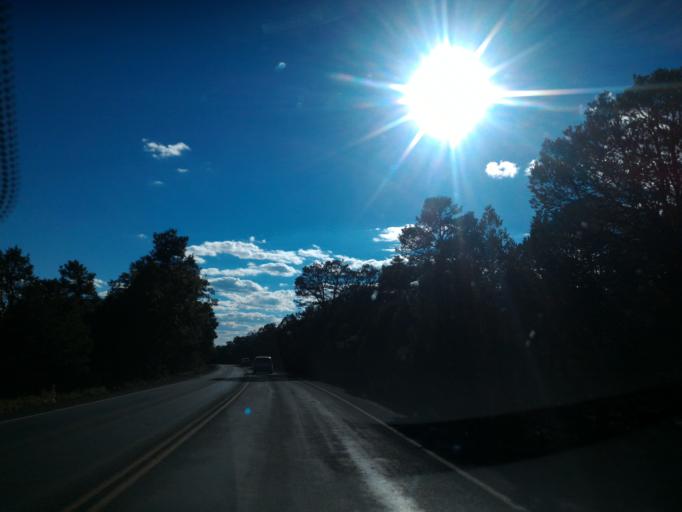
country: US
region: Arizona
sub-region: Coconino County
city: Grand Canyon
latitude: 36.0471
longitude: -112.1151
